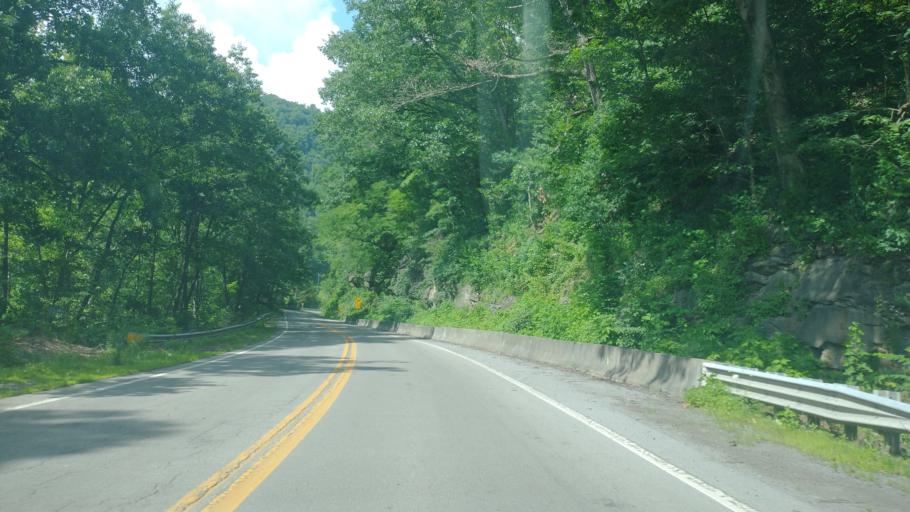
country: US
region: West Virginia
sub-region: McDowell County
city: Welch
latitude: 37.4074
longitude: -81.4635
